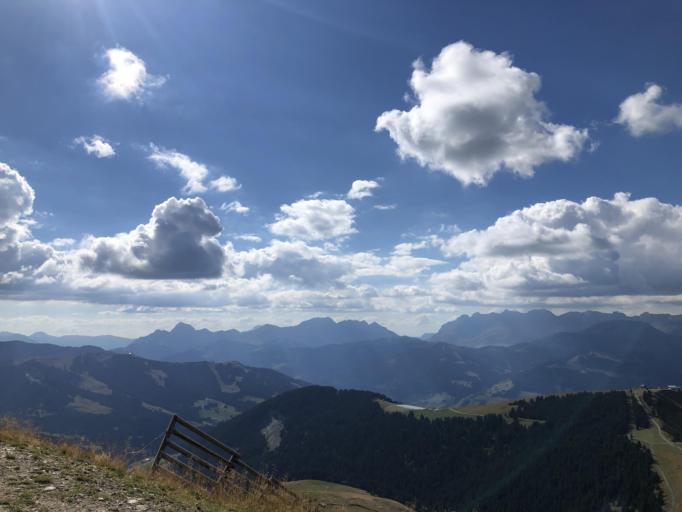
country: FR
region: Rhone-Alpes
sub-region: Departement de la Haute-Savoie
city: Les Contamines-Montjoie
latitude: 45.8382
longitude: 6.6940
